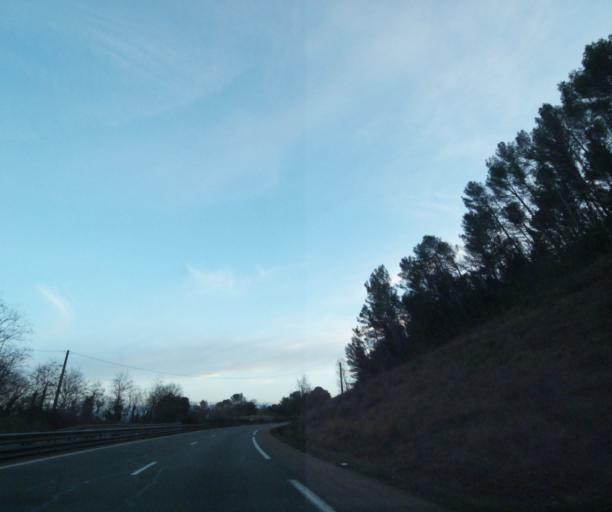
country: FR
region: Provence-Alpes-Cote d'Azur
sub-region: Departement du Var
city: Trans-en-Provence
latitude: 43.4926
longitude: 6.5051
